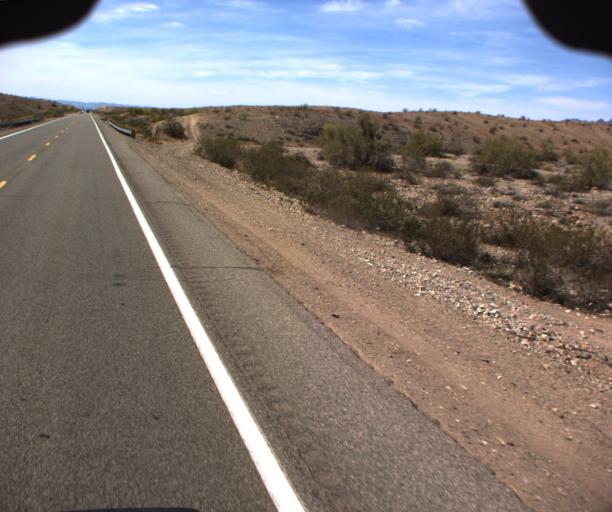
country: US
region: Arizona
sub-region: Mohave County
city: Lake Havasu City
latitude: 34.4369
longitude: -114.2237
